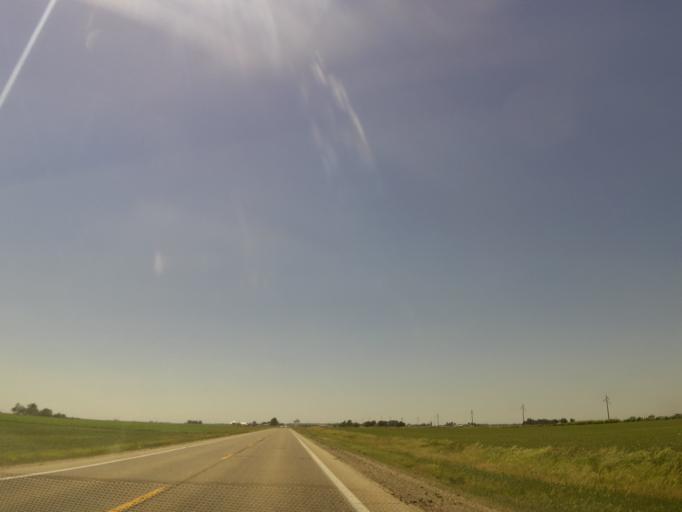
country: US
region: Illinois
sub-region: Woodford County
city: El Paso
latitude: 40.7386
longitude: -88.9560
